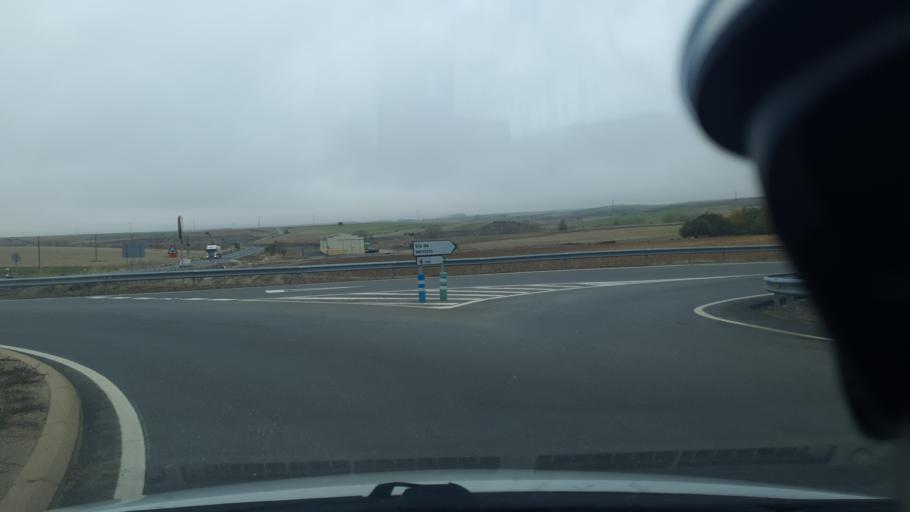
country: ES
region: Castille and Leon
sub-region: Provincia de Segovia
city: Encinillas
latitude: 41.0033
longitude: -4.1525
